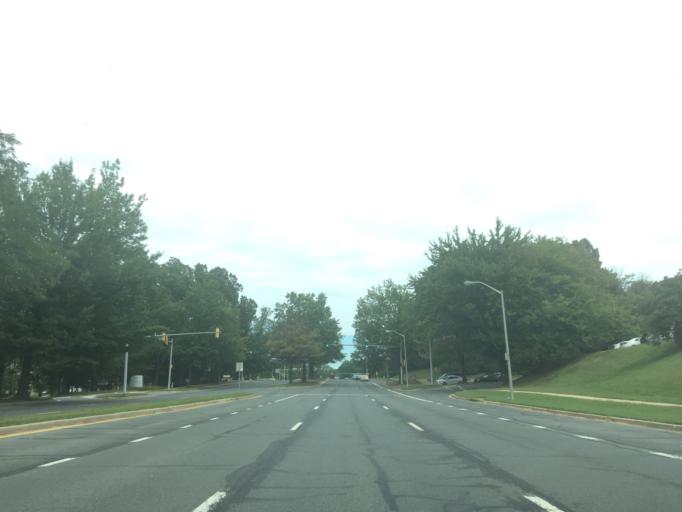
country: US
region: Maryland
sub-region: Montgomery County
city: Gaithersburg
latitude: 39.1562
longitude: -77.2067
